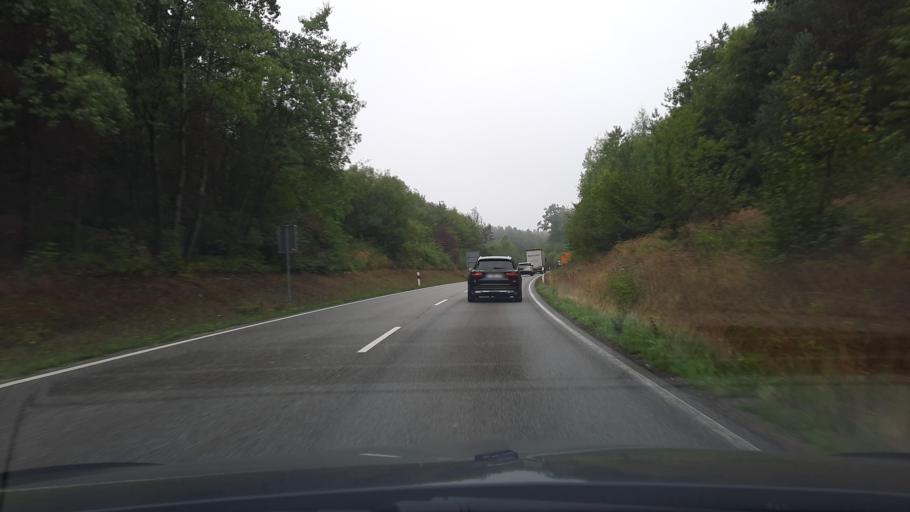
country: DE
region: Rheinland-Pfalz
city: Malbergweich
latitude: 50.0419
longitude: 6.5299
